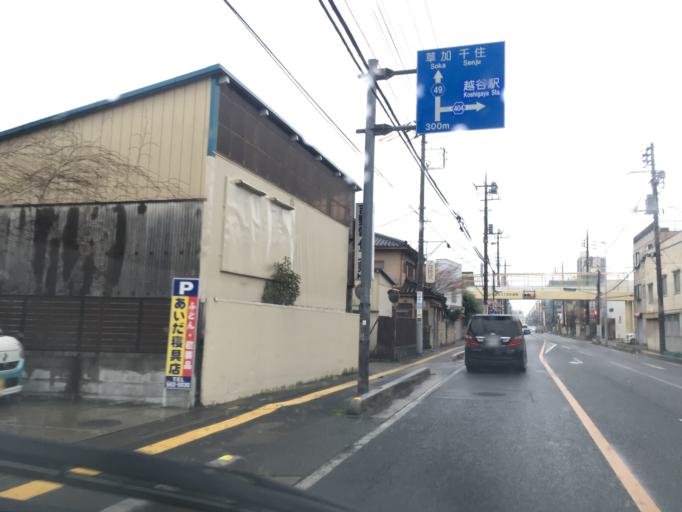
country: JP
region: Saitama
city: Koshigaya
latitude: 35.8936
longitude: 139.7874
